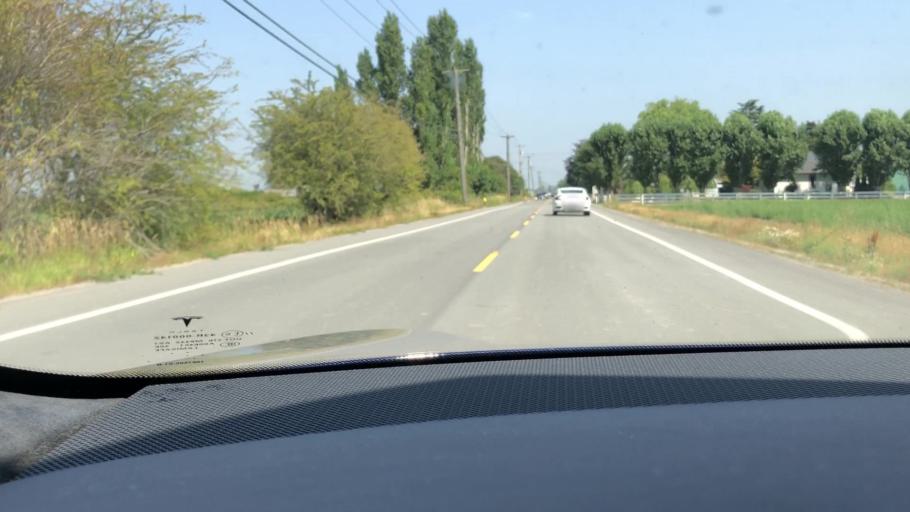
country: CA
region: British Columbia
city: Ladner
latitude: 49.0468
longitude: -123.0797
